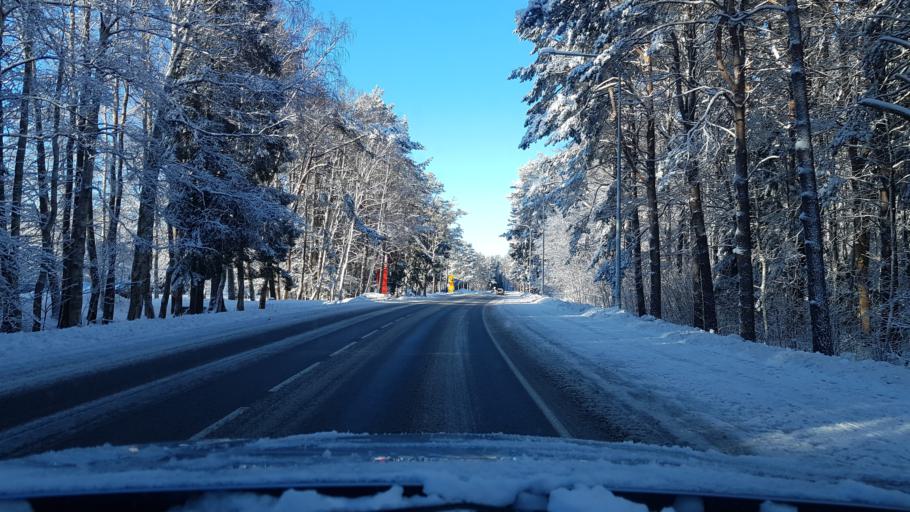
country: EE
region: Hiiumaa
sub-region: Kaerdla linn
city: Kardla
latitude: 58.9944
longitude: 22.7266
